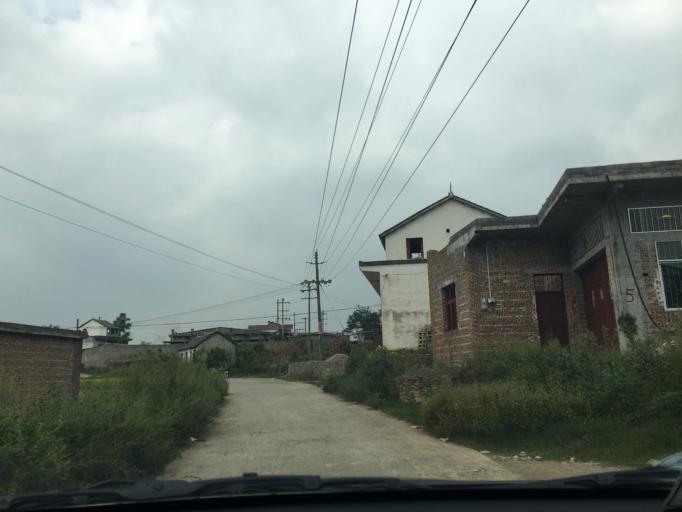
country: CN
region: Guizhou Sheng
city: Anshun
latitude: 25.5714
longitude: 105.6186
